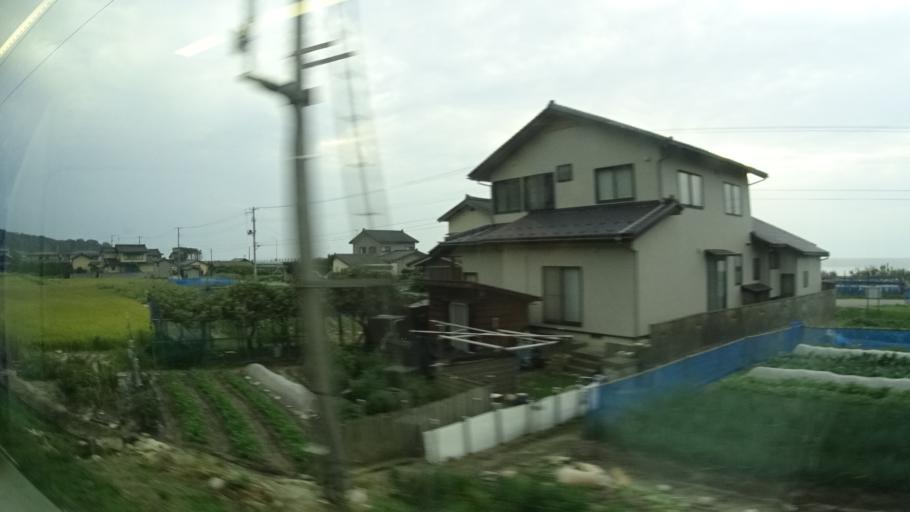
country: JP
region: Niigata
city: Murakami
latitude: 38.2798
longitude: 139.4504
